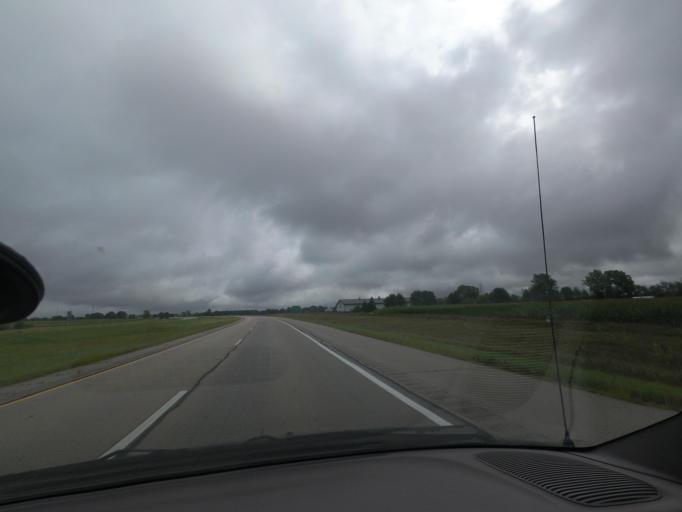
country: US
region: Illinois
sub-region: Piatt County
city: Monticello
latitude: 40.0310
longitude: -88.6093
